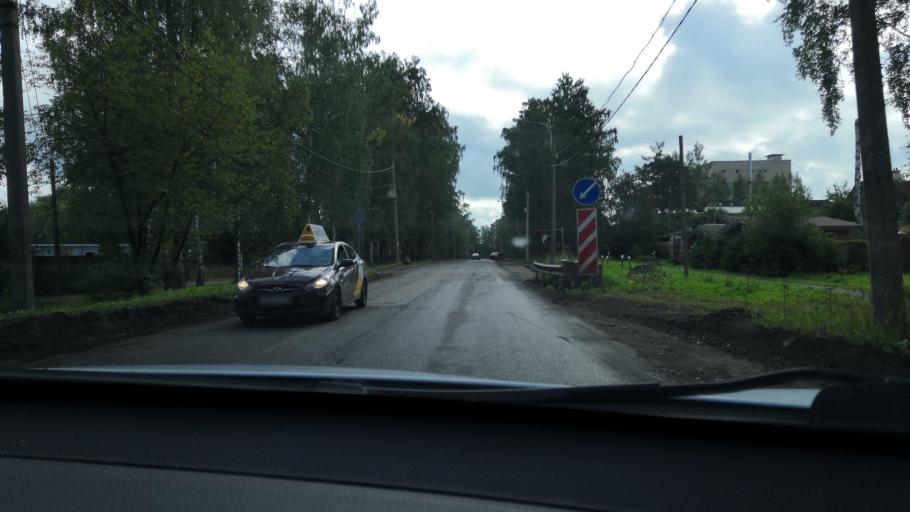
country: RU
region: St.-Petersburg
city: Tyarlevo
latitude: 59.7121
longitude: 30.4470
